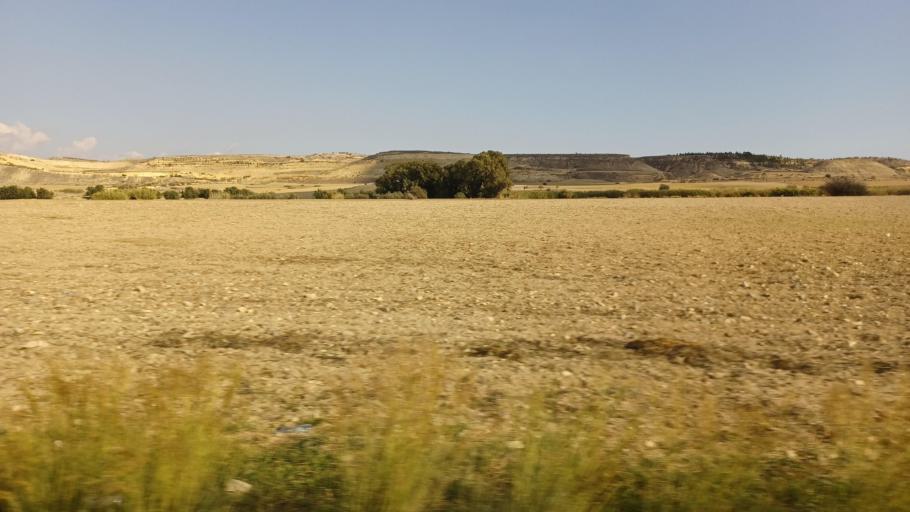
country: CY
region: Larnaka
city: Voroklini
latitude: 34.9866
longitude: 33.6264
